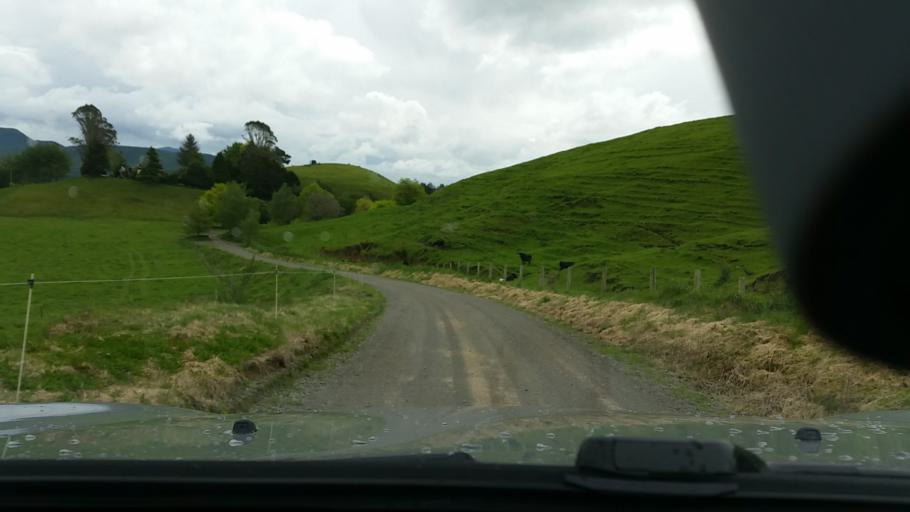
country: NZ
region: Waikato
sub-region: Taupo District
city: Taupo
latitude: -38.4301
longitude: 176.1561
